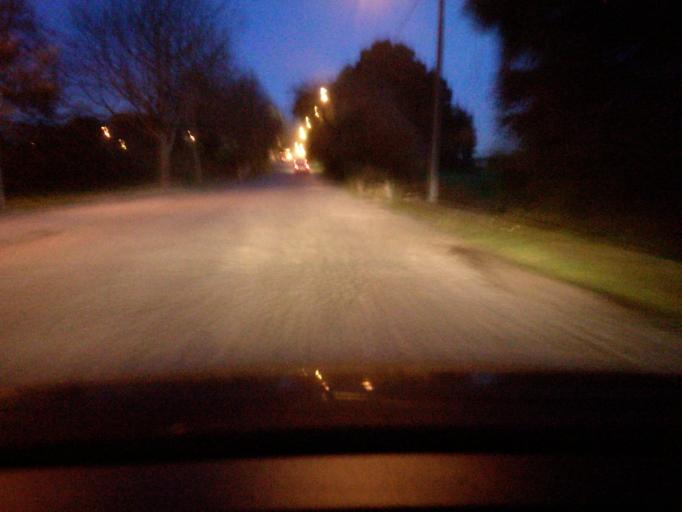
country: PT
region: Porto
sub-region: Maia
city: Gemunde
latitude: 41.2465
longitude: -8.6529
